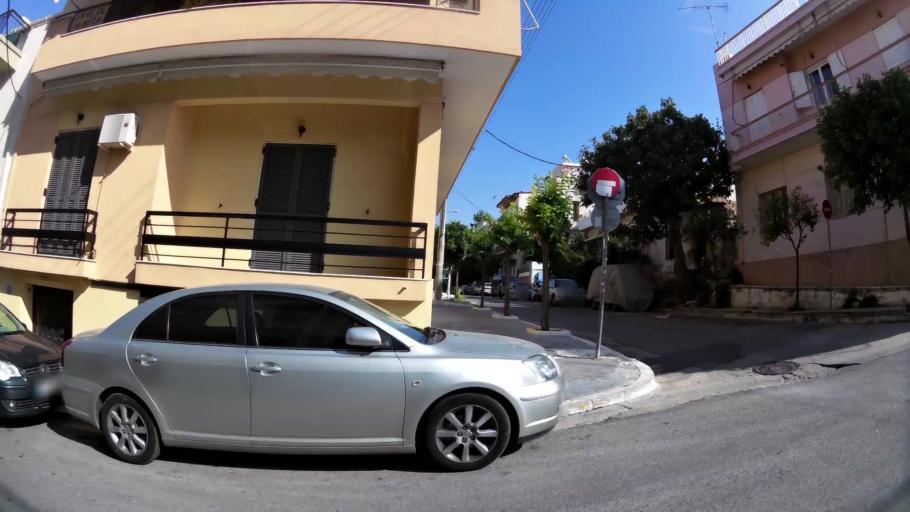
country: GR
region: Attica
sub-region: Nomos Piraios
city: Keratsini
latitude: 37.9578
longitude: 23.6216
